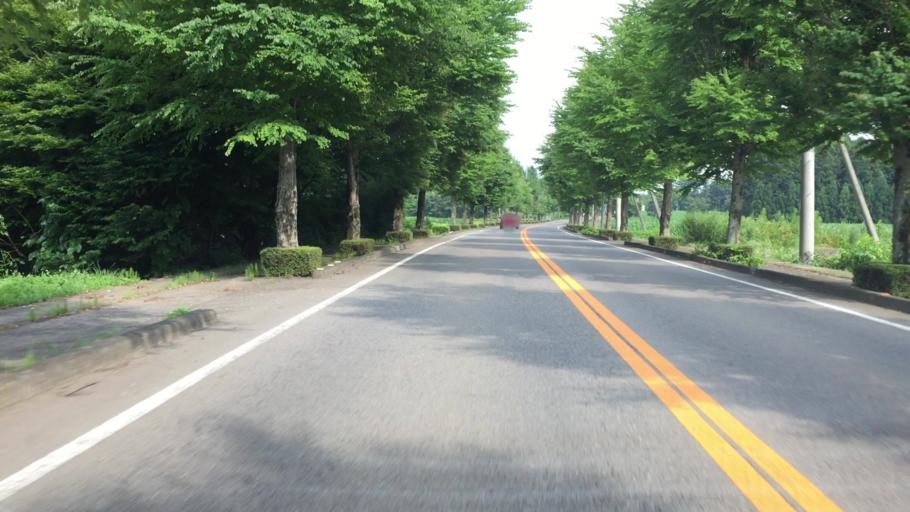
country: JP
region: Tochigi
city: Kuroiso
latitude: 36.9866
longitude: 139.9554
